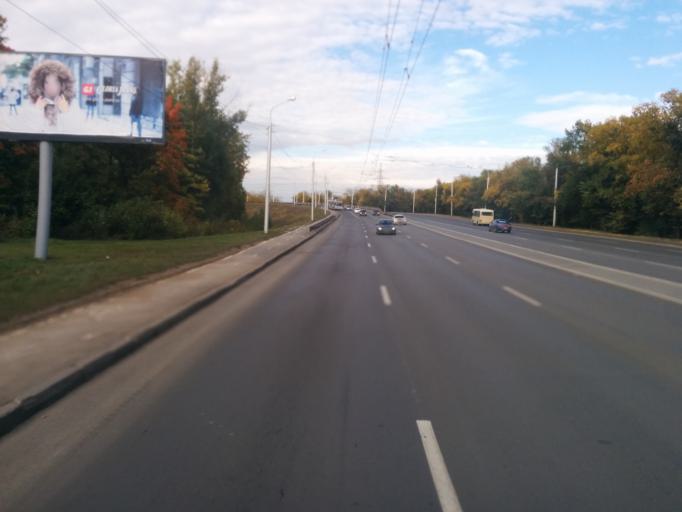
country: RU
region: Bashkortostan
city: Ufa
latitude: 54.8047
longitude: 56.0481
